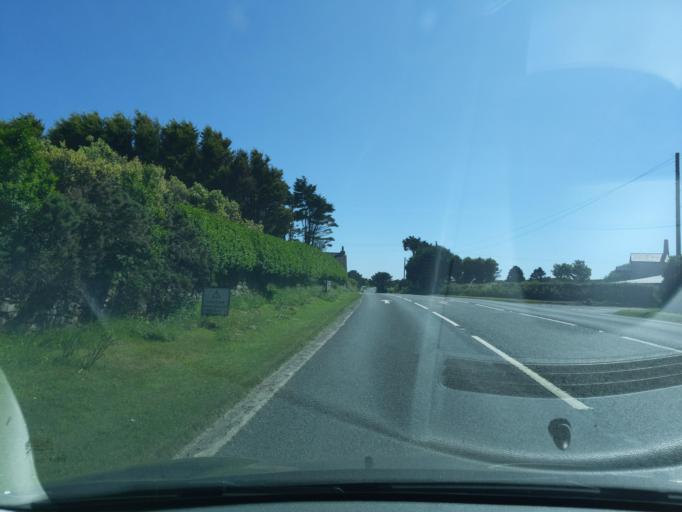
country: GB
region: England
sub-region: Cornwall
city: Wendron
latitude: 50.1401
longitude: -5.2185
